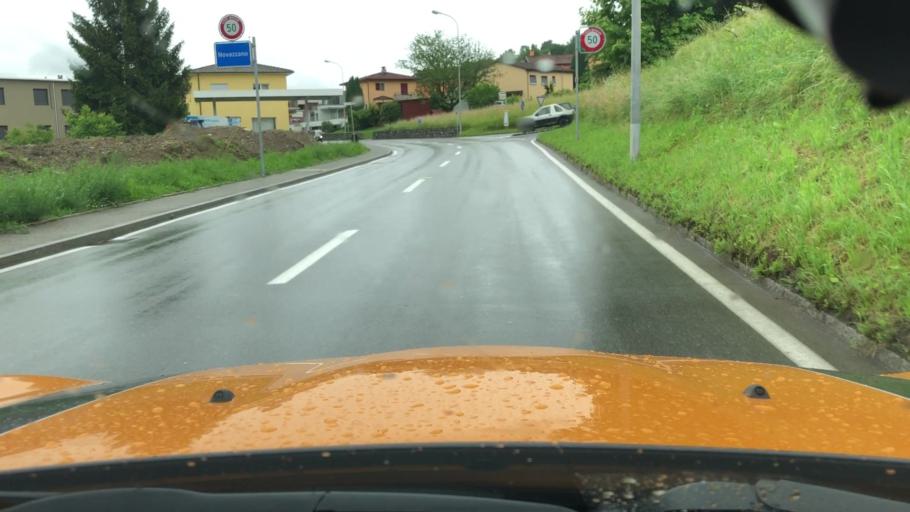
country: CH
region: Ticino
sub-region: Mendrisio District
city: Novazzano
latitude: 45.8441
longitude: 8.9718
